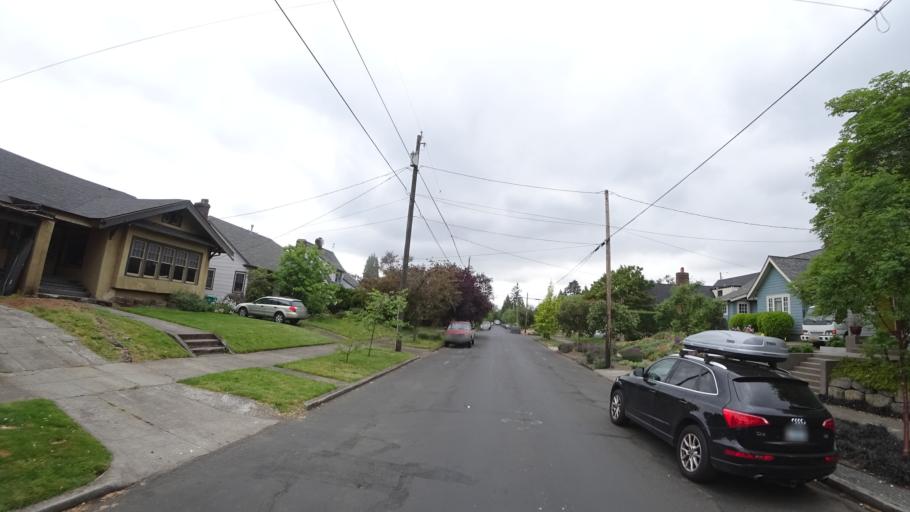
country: US
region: Oregon
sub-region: Multnomah County
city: Portland
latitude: 45.5449
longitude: -122.6188
